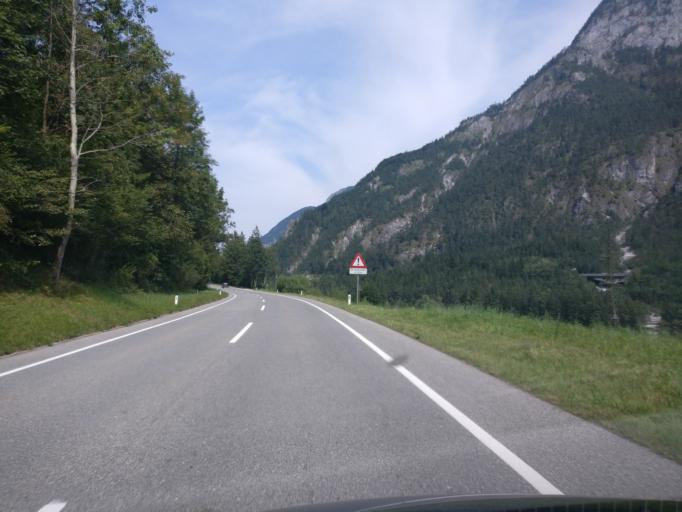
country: AT
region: Salzburg
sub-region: Politischer Bezirk Sankt Johann im Pongau
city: Werfen
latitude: 47.5091
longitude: 13.1671
